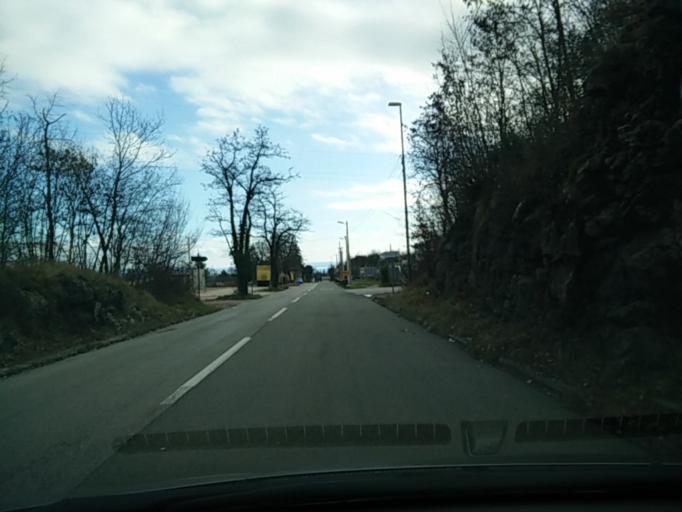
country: HR
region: Primorsko-Goranska
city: Matulji
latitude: 45.3670
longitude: 14.3114
